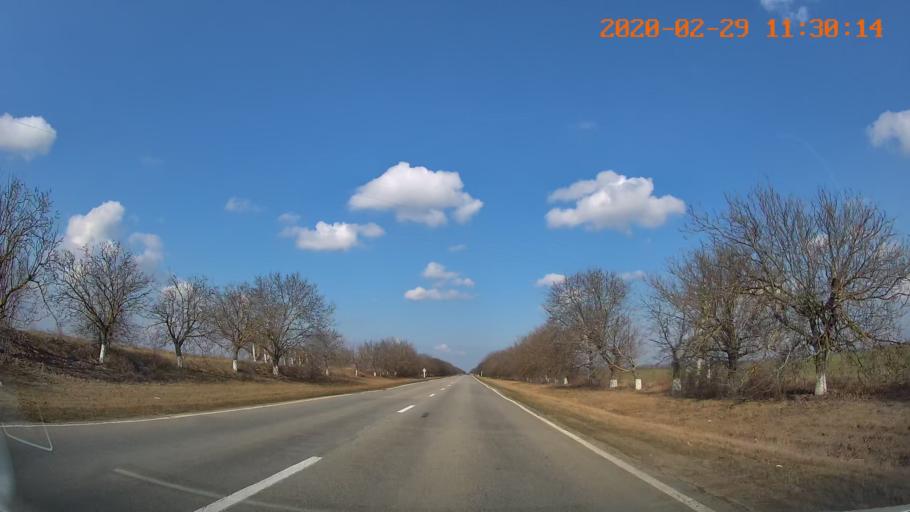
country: MD
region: Telenesti
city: Cocieri
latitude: 47.5067
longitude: 29.1172
